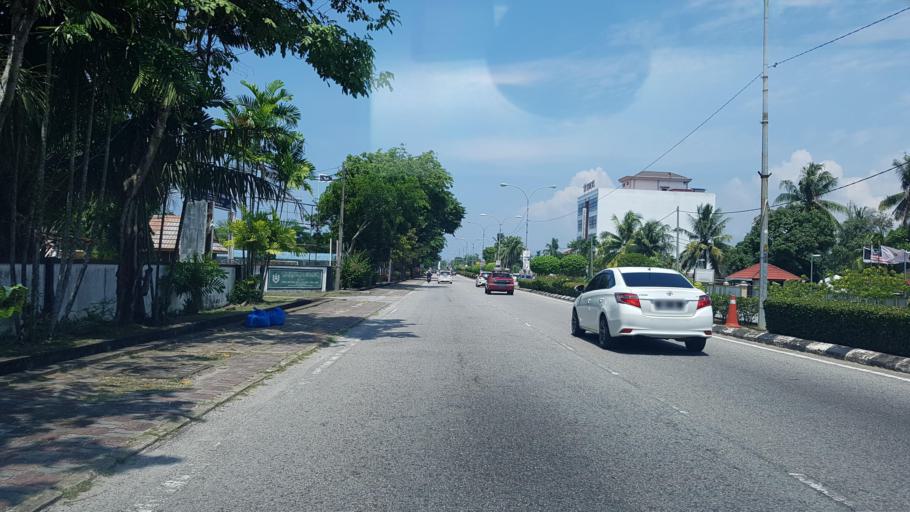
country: MY
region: Terengganu
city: Kuala Terengganu
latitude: 5.3122
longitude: 103.1559
